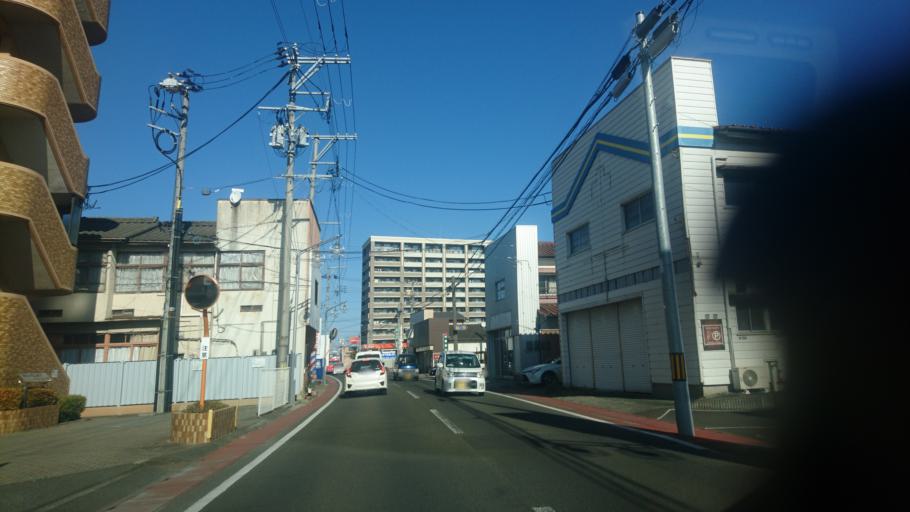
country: JP
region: Miyagi
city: Iwanuma
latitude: 38.1691
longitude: 140.8856
